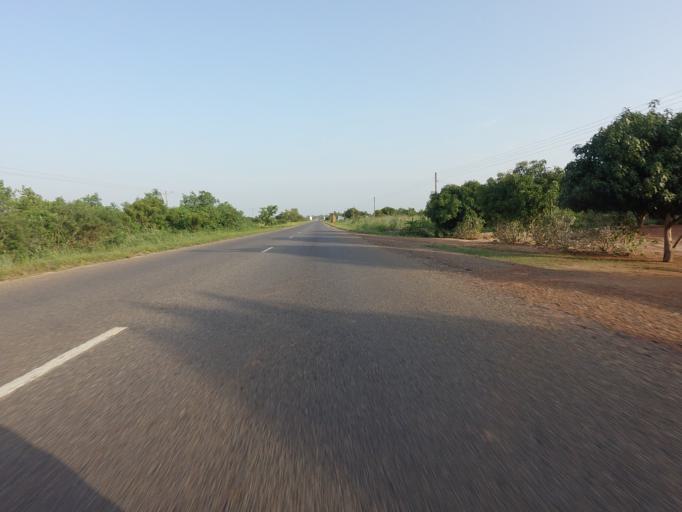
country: GH
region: Volta
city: Anloga
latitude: 6.0098
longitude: 0.6681
